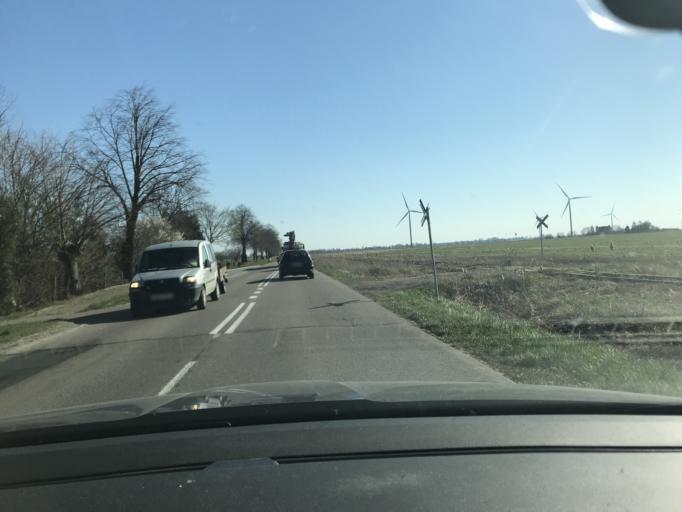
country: PL
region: Pomeranian Voivodeship
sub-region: Powiat nowodworski
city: Nowy Dwor Gdanski
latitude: 54.2630
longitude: 19.1361
